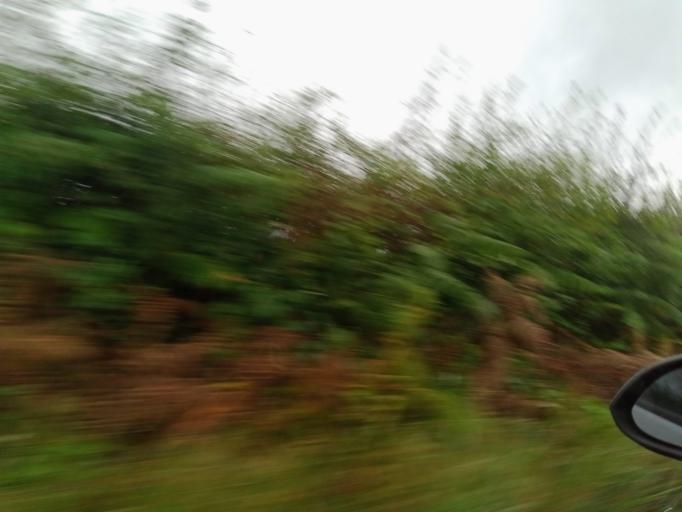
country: IE
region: Leinster
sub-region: Laois
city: Mountmellick
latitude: 53.1168
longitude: -7.3619
